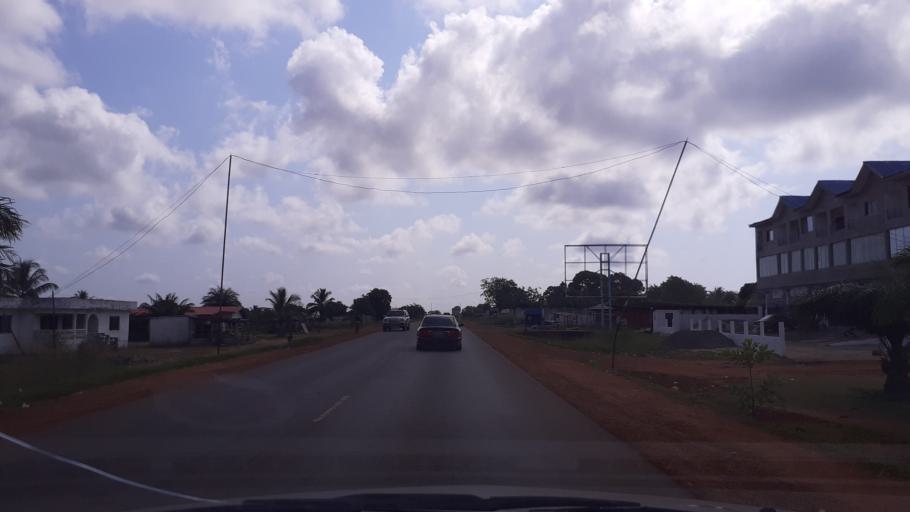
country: LR
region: Montserrado
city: Monrovia
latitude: 6.2254
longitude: -10.6163
